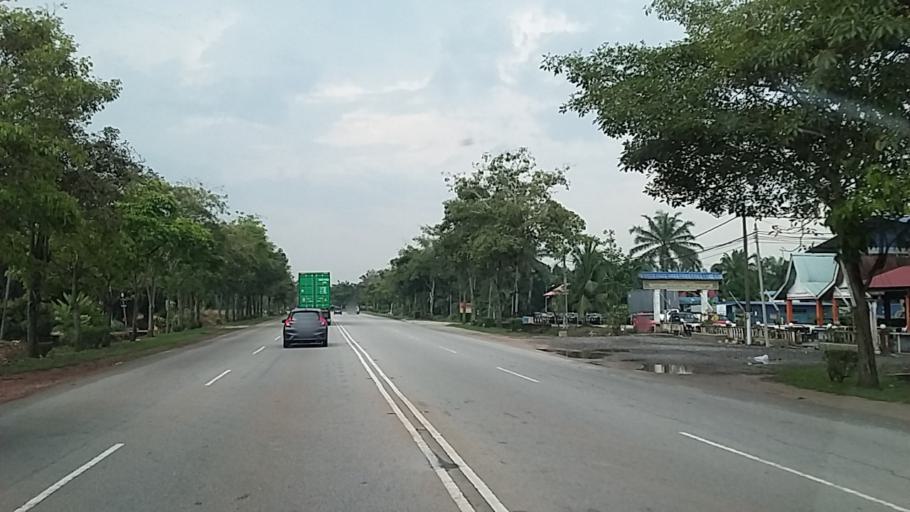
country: MY
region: Johor
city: Parit Raja
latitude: 1.8744
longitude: 103.1389
